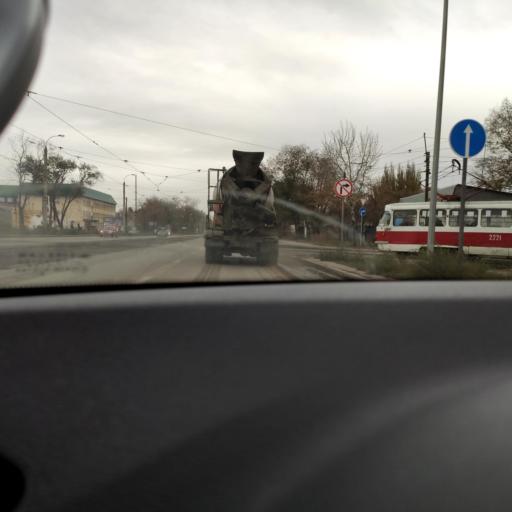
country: RU
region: Samara
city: Smyshlyayevka
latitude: 53.1928
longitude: 50.2939
